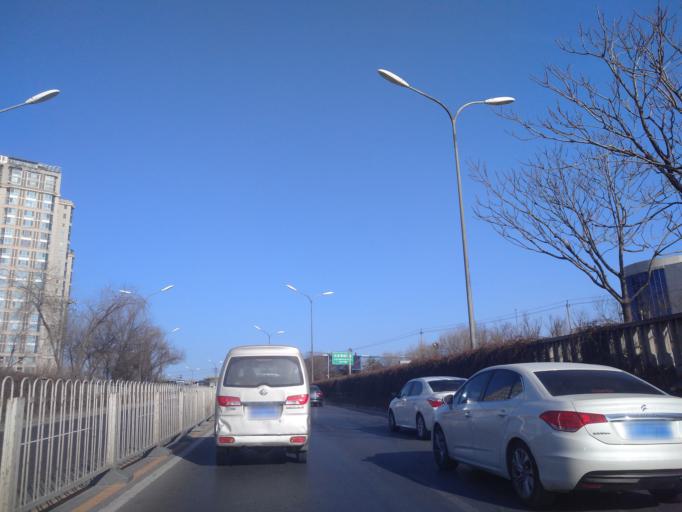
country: CN
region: Beijing
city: Jiugong
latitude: 39.8326
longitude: 116.4699
